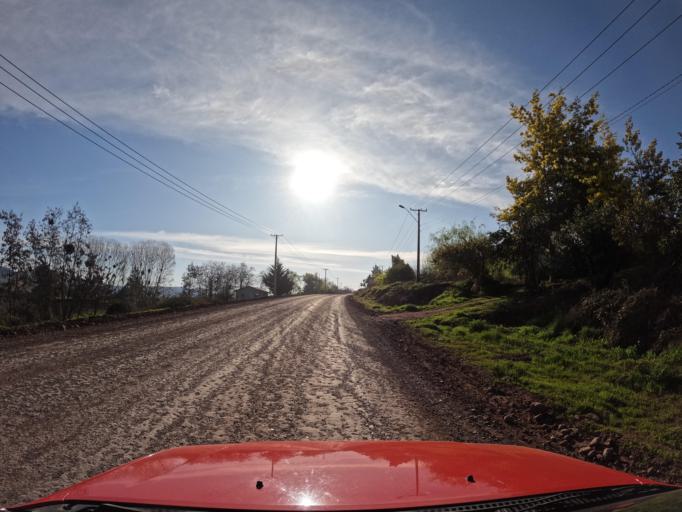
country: CL
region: Maule
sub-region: Provincia de Curico
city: Teno
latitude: -34.9659
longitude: -70.9506
